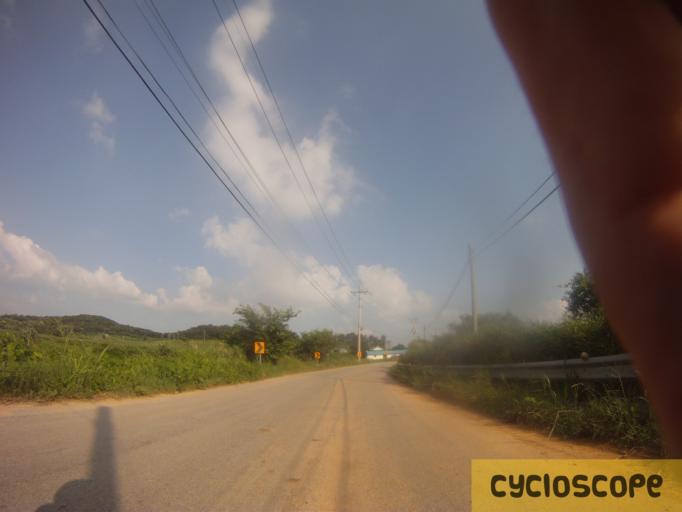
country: KR
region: Jeollabuk-do
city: Koch'ang
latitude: 35.4403
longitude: 126.6607
